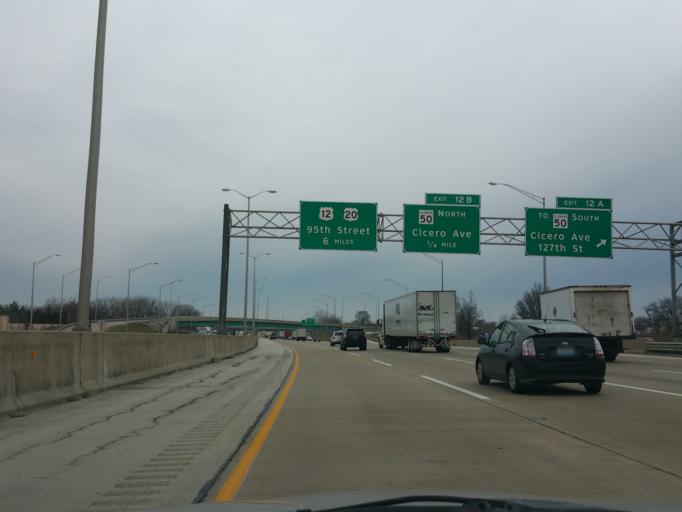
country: US
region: Illinois
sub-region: Cook County
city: Alsip
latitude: 41.6587
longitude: -87.7305
